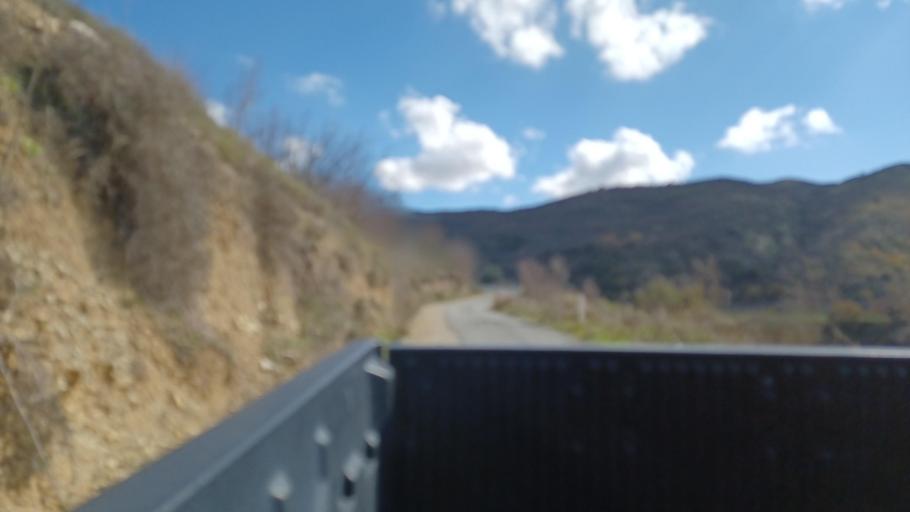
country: CY
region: Limassol
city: Pachna
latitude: 34.8157
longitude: 32.7331
